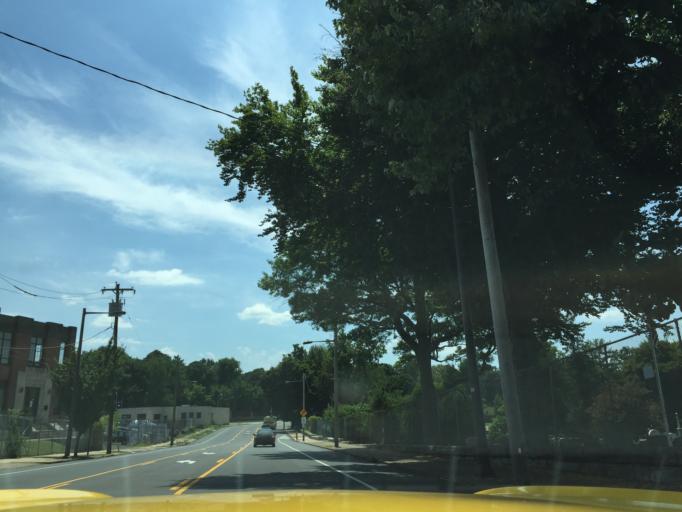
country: US
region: Pennsylvania
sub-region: Montgomery County
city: Bala-Cynwyd
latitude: 40.0027
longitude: -75.1872
